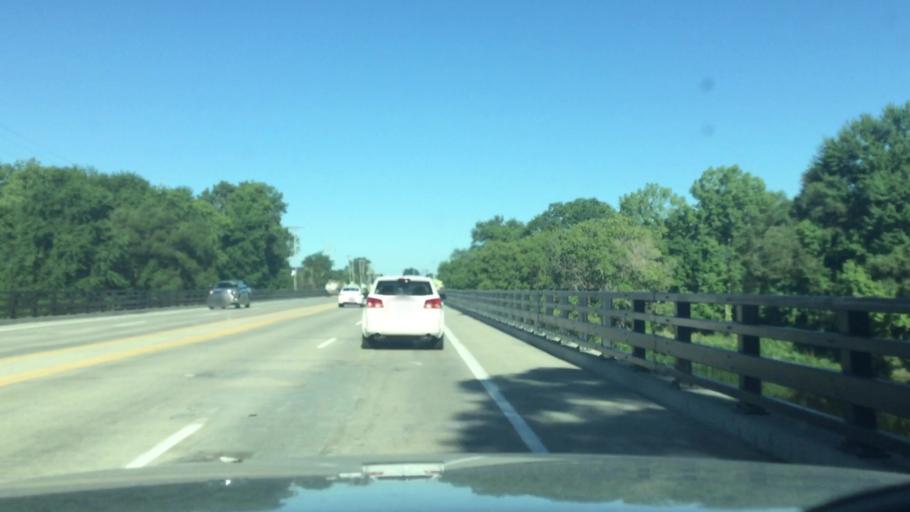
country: US
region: Michigan
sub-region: Saginaw County
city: Shields
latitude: 43.4157
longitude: -84.0446
